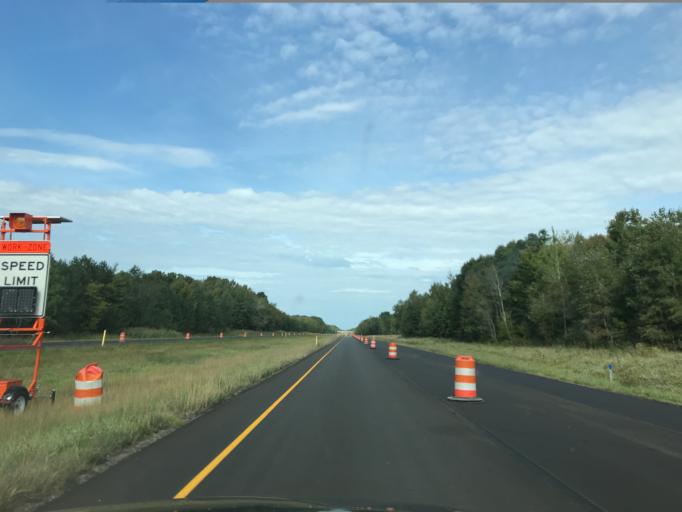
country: US
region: Ohio
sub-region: Ashtabula County
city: Jefferson
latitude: 41.7693
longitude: -80.7238
